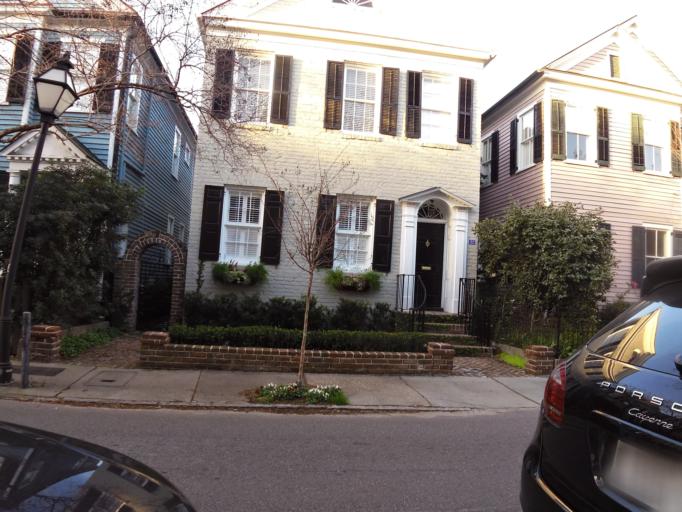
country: US
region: South Carolina
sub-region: Charleston County
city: Charleston
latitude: 32.7750
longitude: -79.9284
